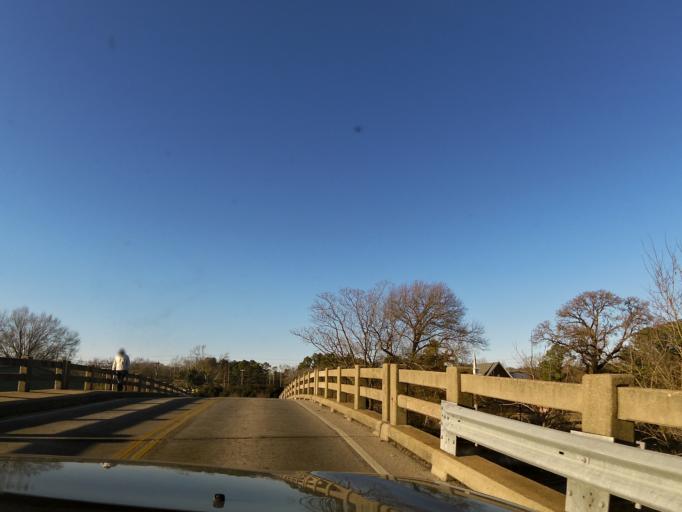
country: US
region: Virginia
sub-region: City of Franklin
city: Franklin
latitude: 36.6827
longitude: -76.9118
